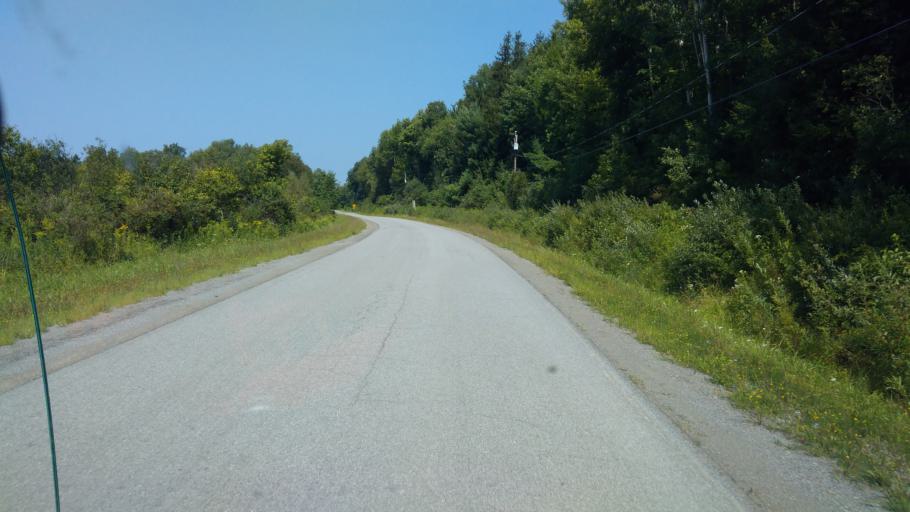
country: US
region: New York
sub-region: Allegany County
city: Belmont
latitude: 42.3196
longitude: -78.0697
